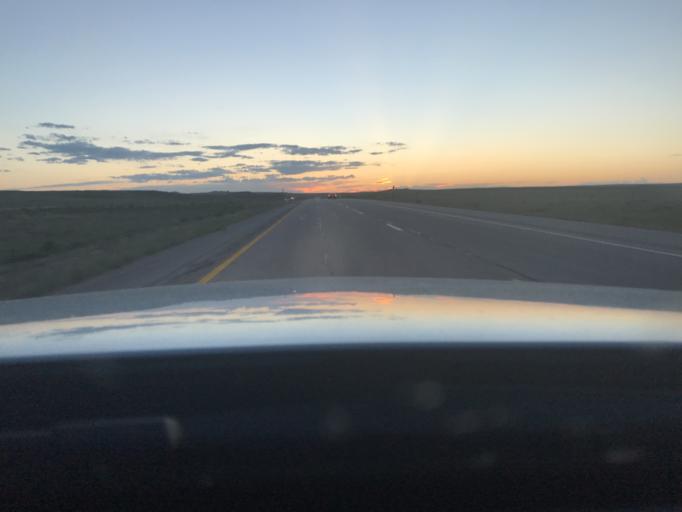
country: US
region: Wyoming
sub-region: Converse County
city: Glenrock
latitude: 42.8312
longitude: -105.8367
